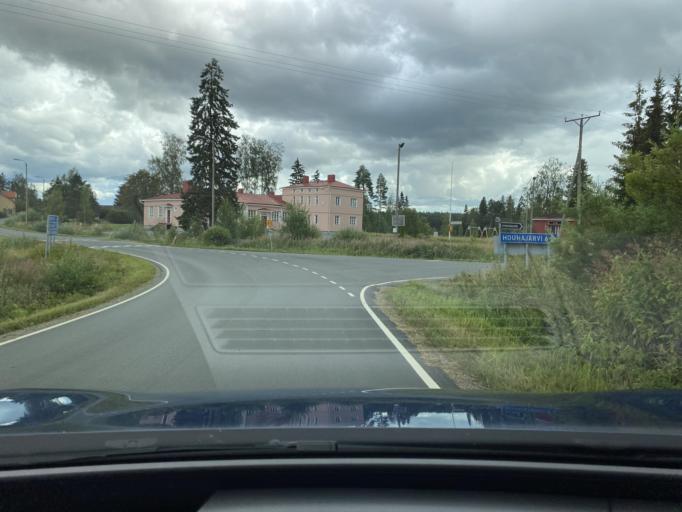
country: FI
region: Pirkanmaa
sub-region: Lounais-Pirkanmaa
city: Punkalaidun
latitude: 61.2335
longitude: 23.1245
